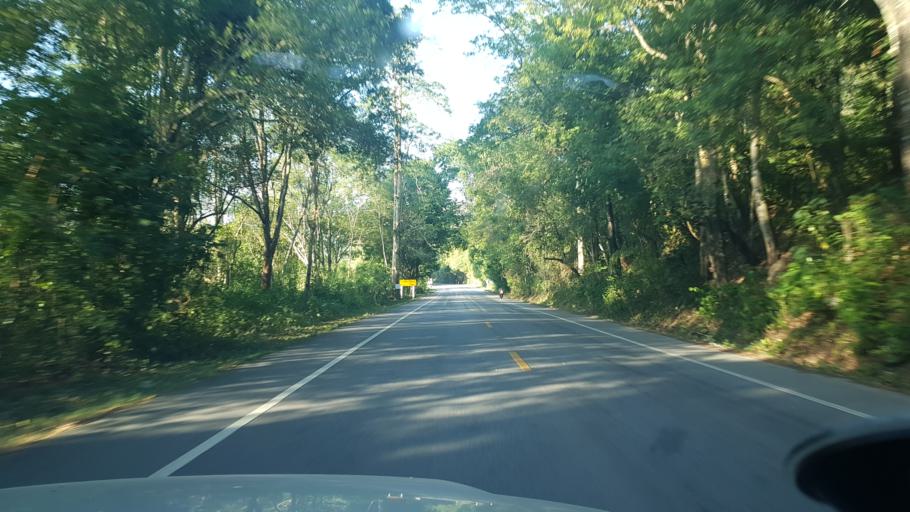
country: TH
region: Khon Kaen
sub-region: Amphoe Phu Pha Man
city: Phu Pha Man
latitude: 16.6497
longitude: 101.7984
